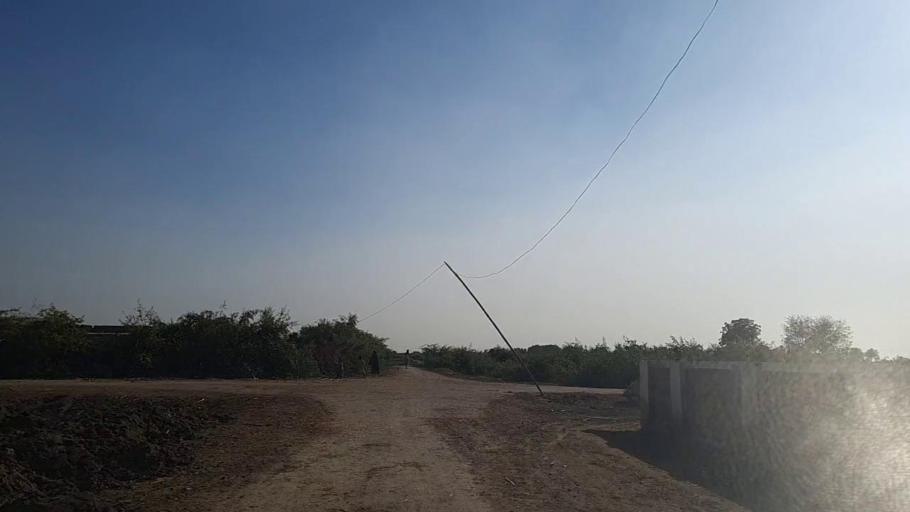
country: PK
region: Sindh
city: Shahpur Chakar
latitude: 26.2151
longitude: 68.6424
